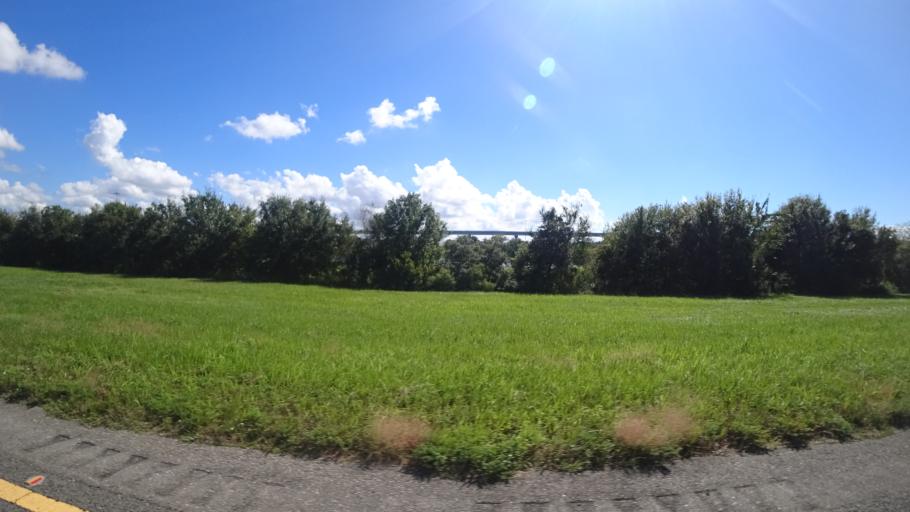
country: US
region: Florida
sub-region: Manatee County
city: Ellenton
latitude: 27.5874
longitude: -82.5164
